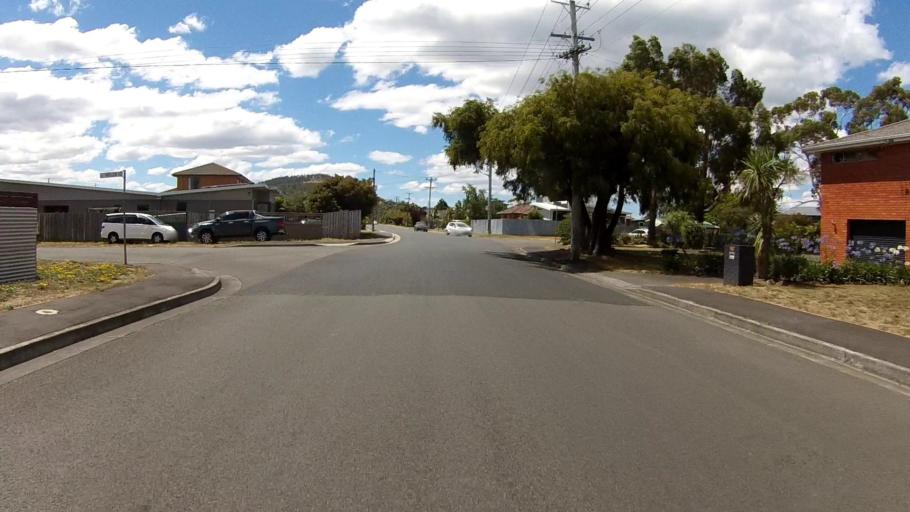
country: AU
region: Tasmania
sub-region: Clarence
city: Lauderdale
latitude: -42.8975
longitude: 147.4963
